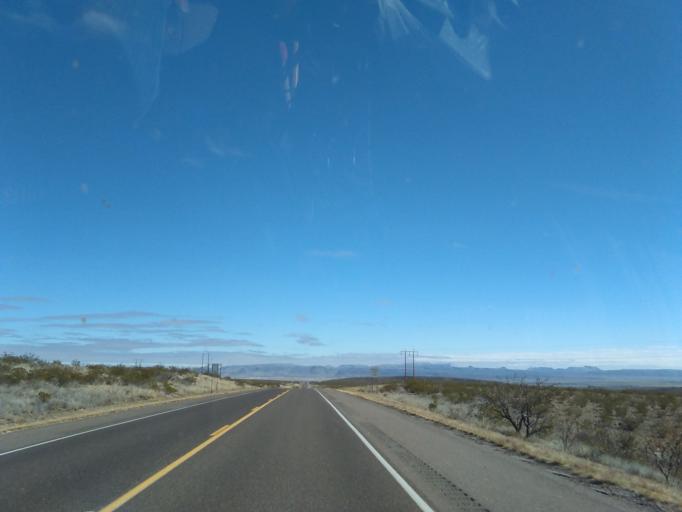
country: US
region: New Mexico
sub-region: Dona Ana County
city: Hatch
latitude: 32.5766
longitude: -107.4329
